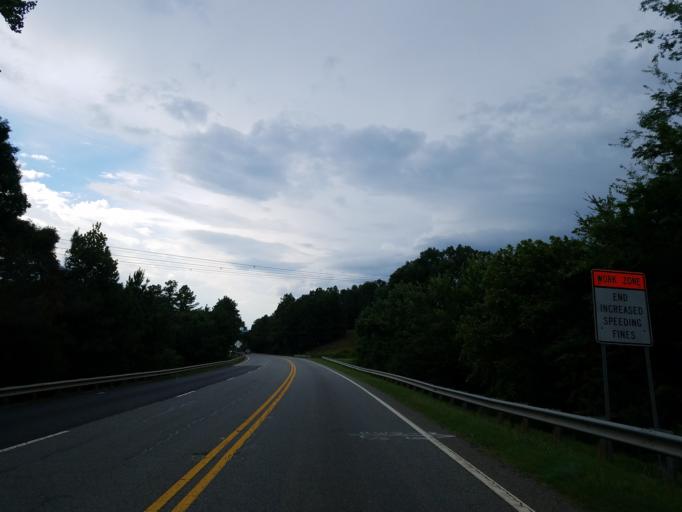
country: US
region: Georgia
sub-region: Bartow County
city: Adairsville
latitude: 34.3267
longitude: -84.8993
